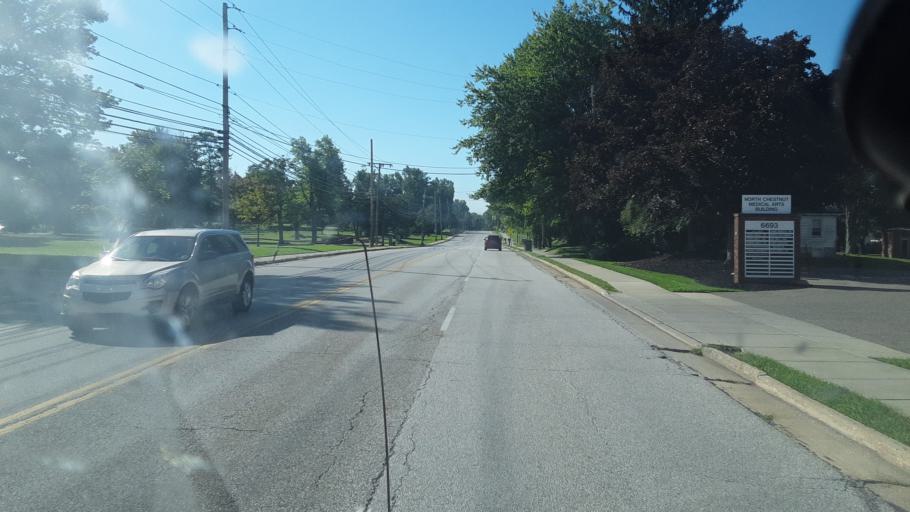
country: US
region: Ohio
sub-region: Portage County
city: Ravenna
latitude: 41.1731
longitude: -81.2448
